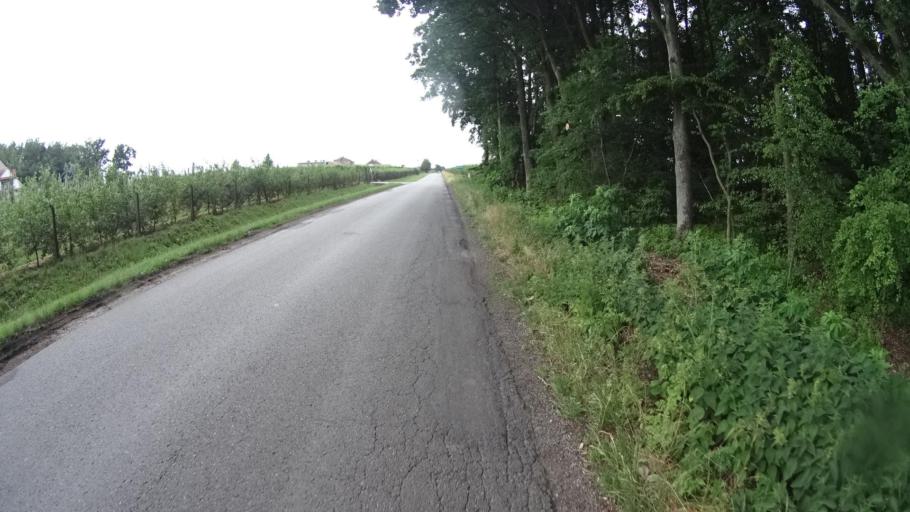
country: PL
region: Masovian Voivodeship
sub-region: Powiat grojecki
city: Goszczyn
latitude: 51.7758
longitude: 20.8536
